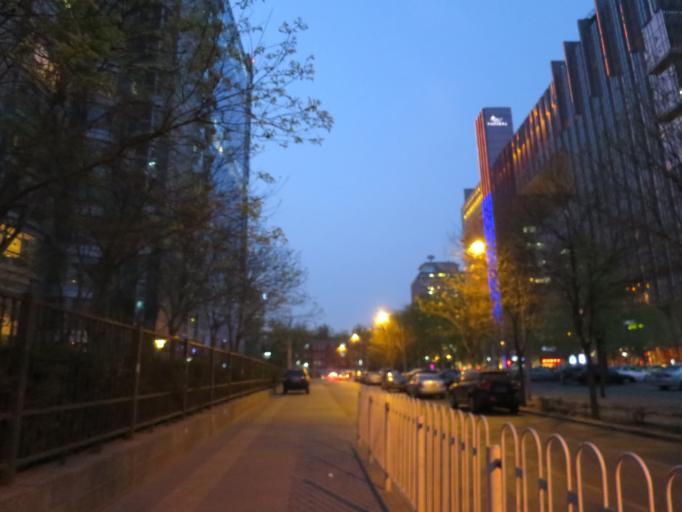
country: CN
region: Beijing
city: Chaowai
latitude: 39.9030
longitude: 116.4449
